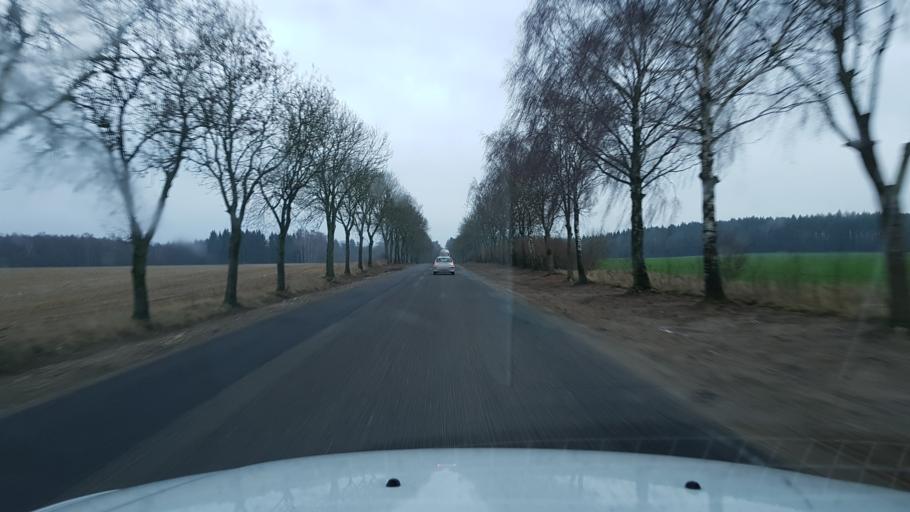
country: PL
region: West Pomeranian Voivodeship
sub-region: Powiat gryficki
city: Gryfice
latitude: 53.8652
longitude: 15.2199
